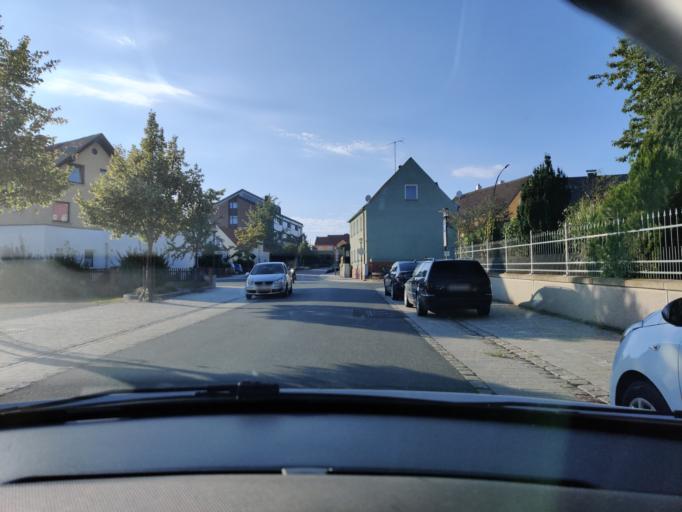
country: DE
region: Bavaria
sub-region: Upper Palatinate
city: Schwarzenfeld
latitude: 49.3903
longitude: 12.1385
